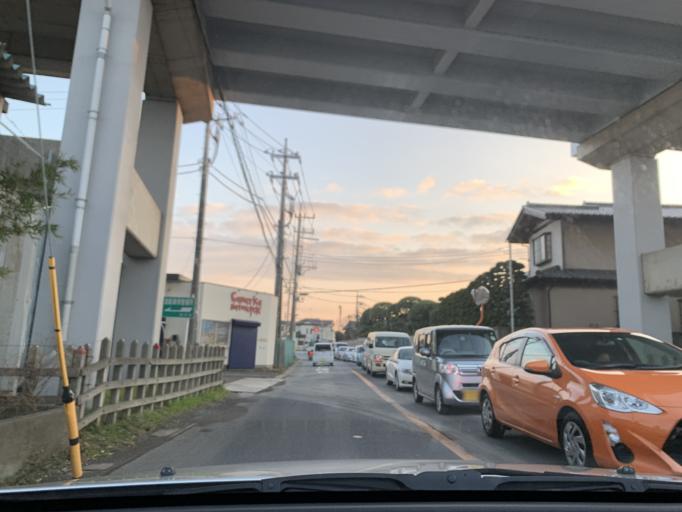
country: JP
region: Chiba
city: Matsudo
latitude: 35.7639
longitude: 139.9196
